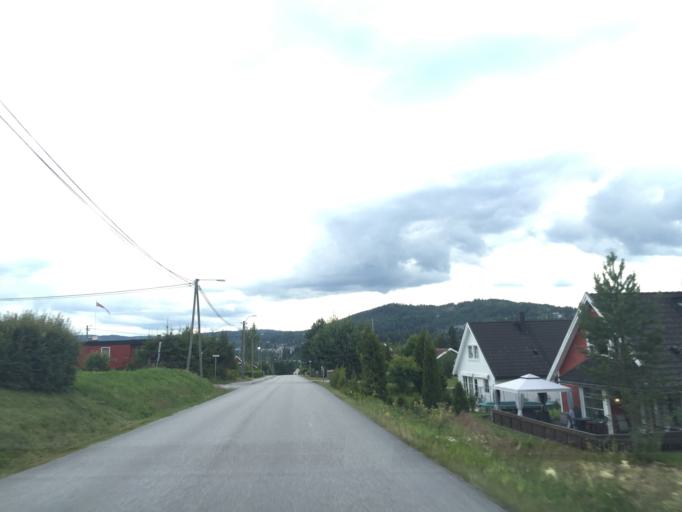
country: NO
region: Hedmark
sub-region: Kongsvinger
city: Kongsvinger
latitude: 60.1854
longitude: 11.9975
